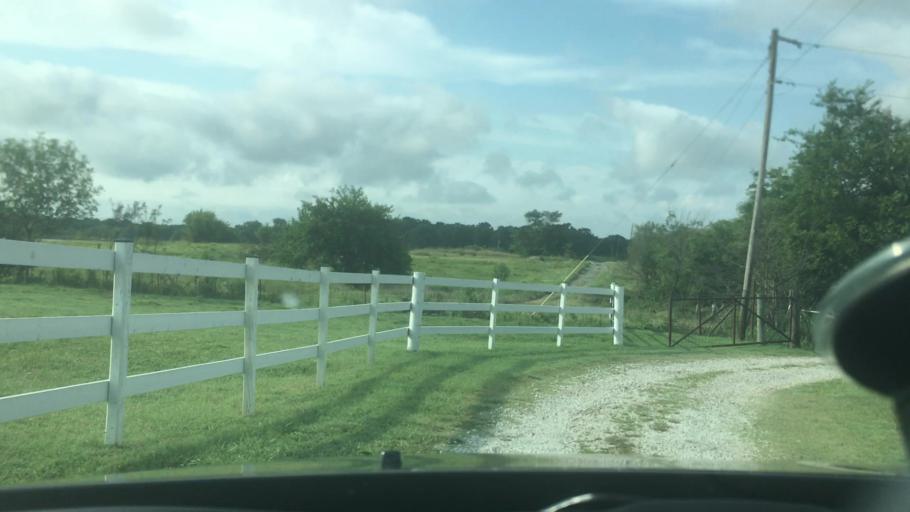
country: US
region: Oklahoma
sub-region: Pontotoc County
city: Ada
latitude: 34.6658
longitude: -96.5253
